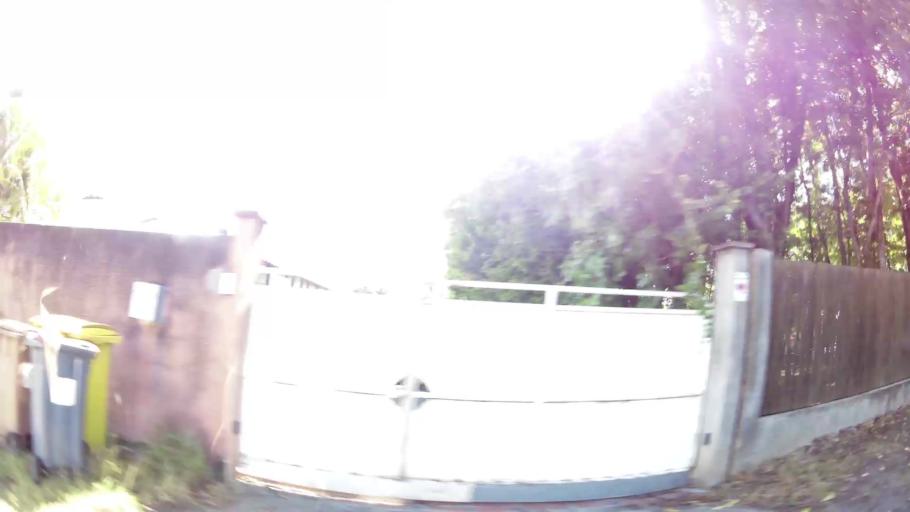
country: MQ
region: Martinique
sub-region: Martinique
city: Les Trois-Ilets
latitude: 14.4715
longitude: -61.0449
